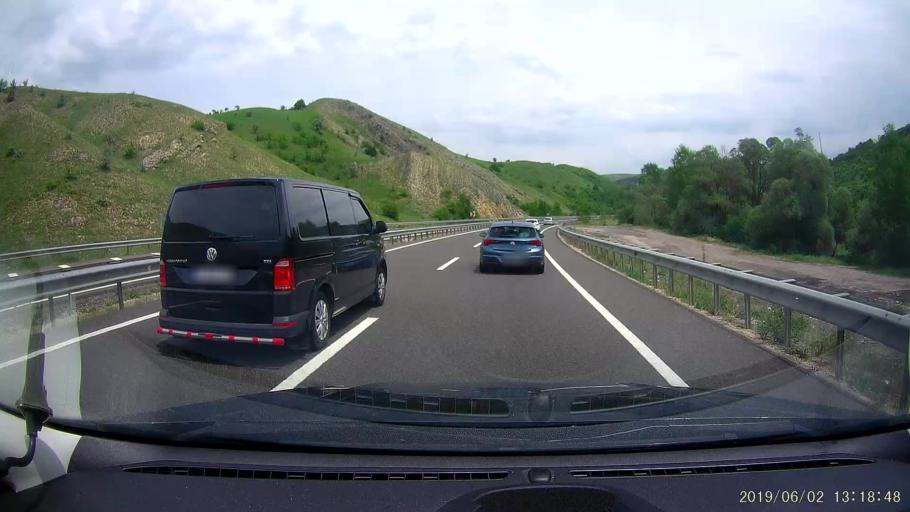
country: TR
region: Cankiri
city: Cerkes
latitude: 40.8341
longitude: 32.7201
